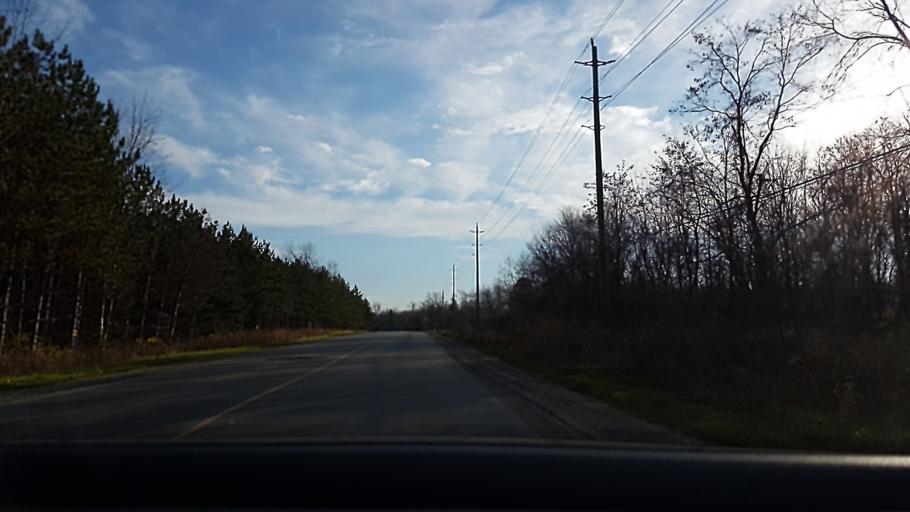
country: CA
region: Ontario
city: Barrie
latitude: 44.3693
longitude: -79.5522
